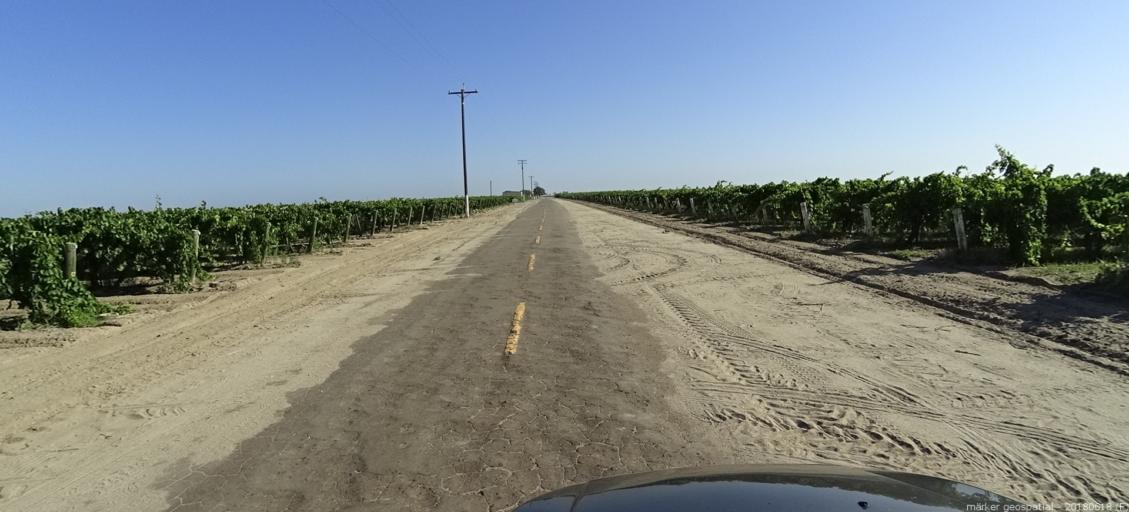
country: US
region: California
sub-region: Fresno County
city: Biola
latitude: 36.8263
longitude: -120.1059
